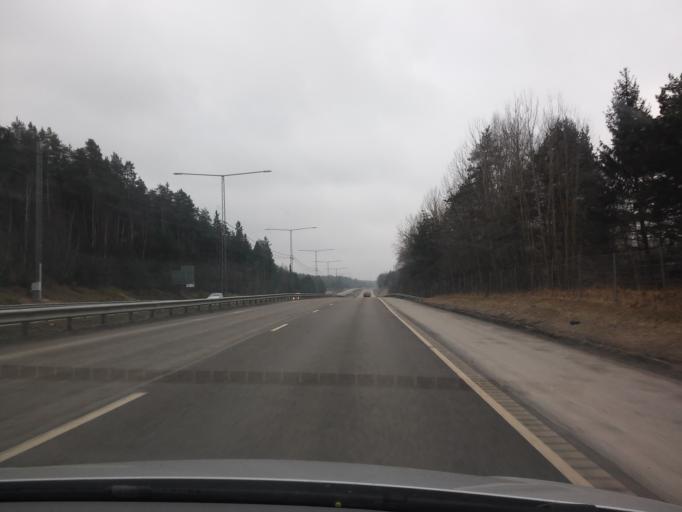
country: SE
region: Stockholm
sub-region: Vallentuna Kommun
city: Vallentuna
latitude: 59.4859
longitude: 18.1652
